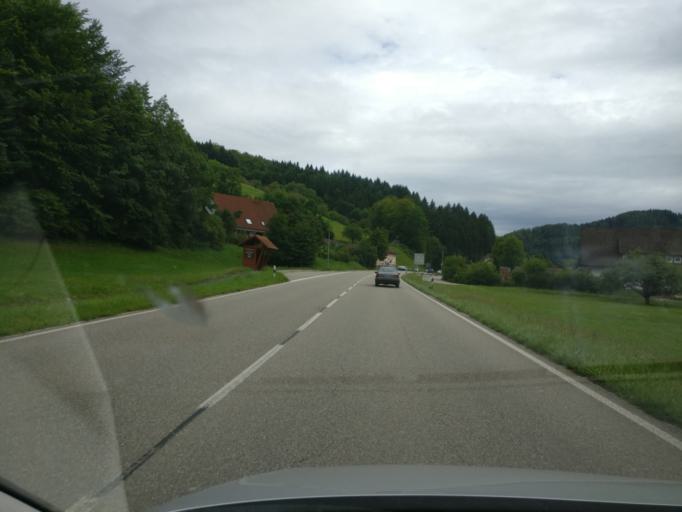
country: DE
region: Baden-Wuerttemberg
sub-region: Freiburg Region
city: Oppenau
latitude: 48.4975
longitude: 8.1405
